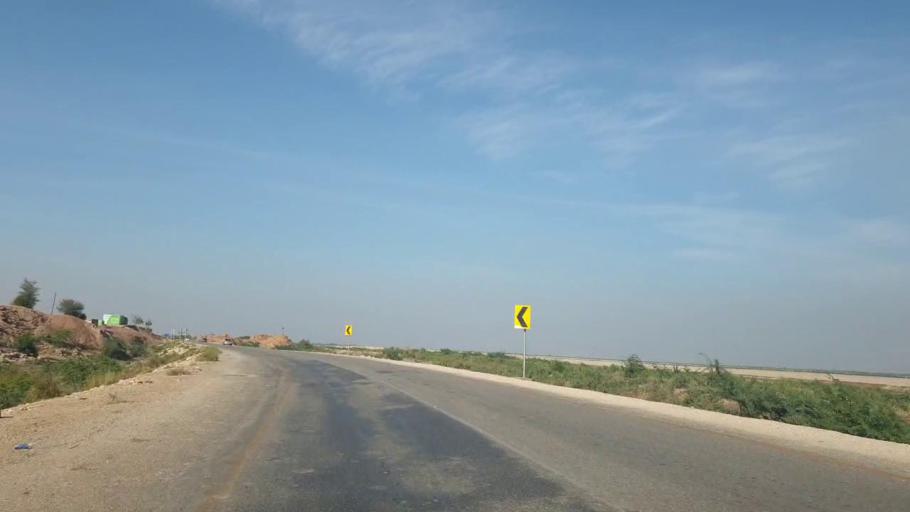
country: PK
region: Sindh
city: Sehwan
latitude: 26.3709
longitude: 67.8742
